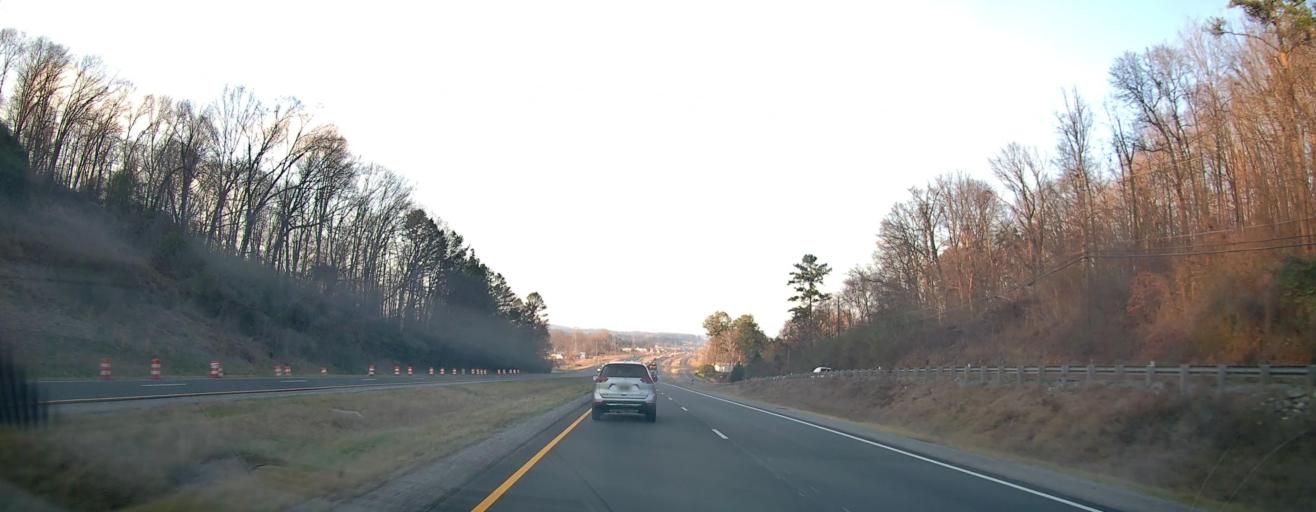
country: US
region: Alabama
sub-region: Calhoun County
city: Alexandria
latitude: 33.7551
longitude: -85.8888
